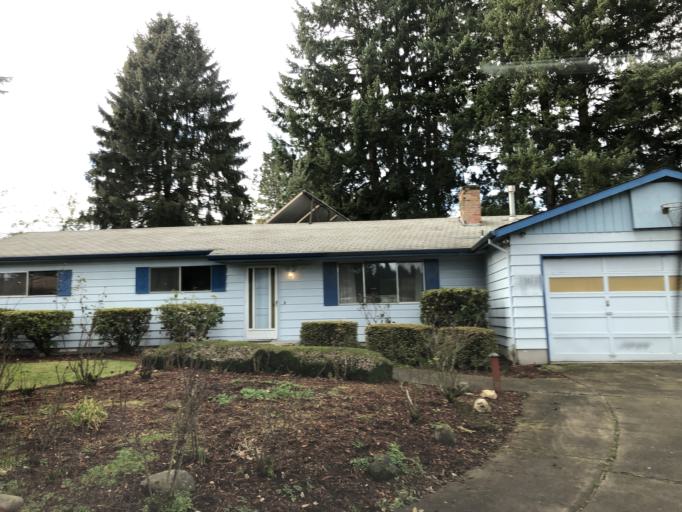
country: US
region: Oregon
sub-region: Washington County
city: Tigard
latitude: 45.4230
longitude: -122.7884
